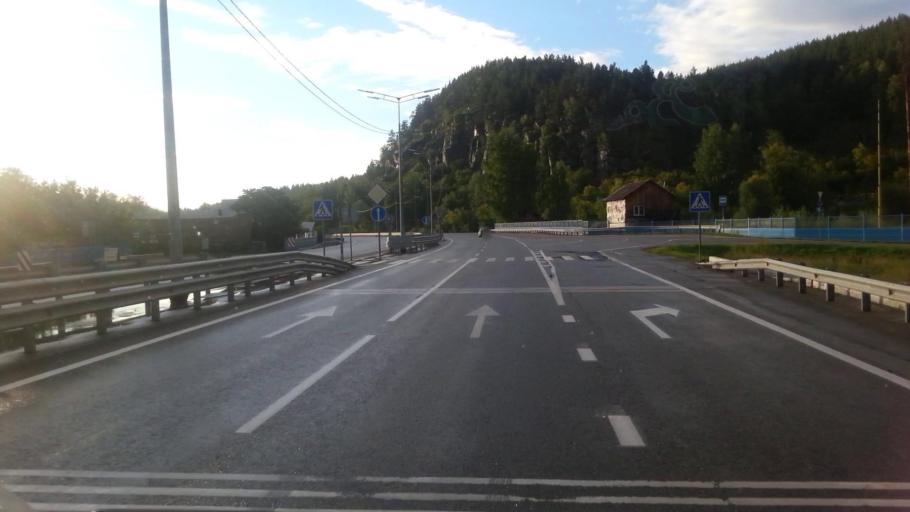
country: RU
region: Altay
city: Souzga
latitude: 51.9176
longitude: 85.8597
